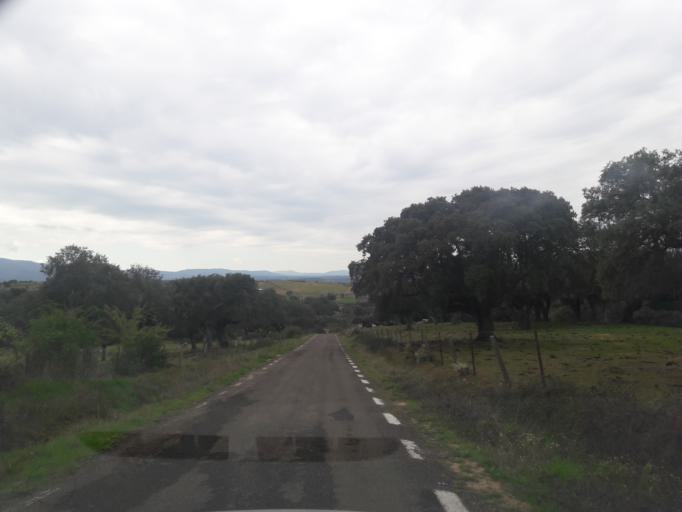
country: ES
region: Castille and Leon
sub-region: Provincia de Salamanca
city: Serradilla del Arroyo
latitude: 40.5090
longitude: -6.4043
